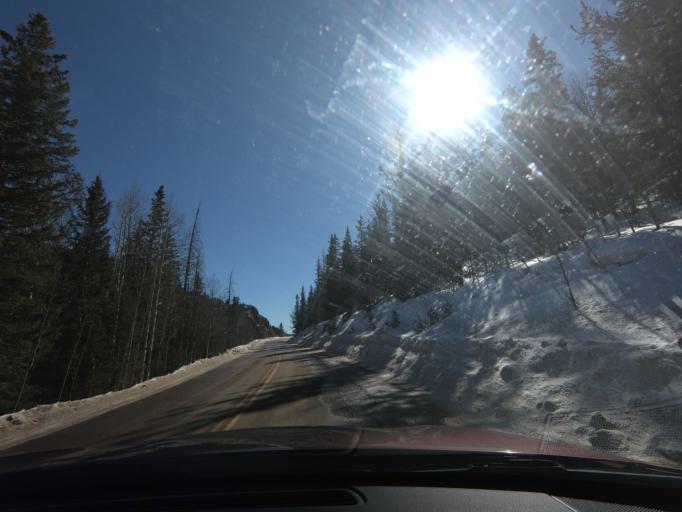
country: US
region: Colorado
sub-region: Teller County
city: Cripple Creek
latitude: 38.7486
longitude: -105.1017
